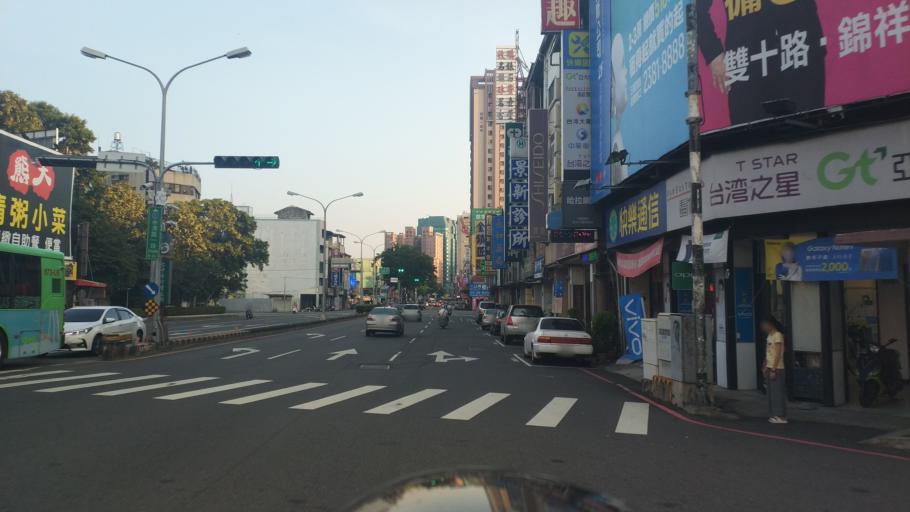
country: TW
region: Taiwan
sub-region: Taichung City
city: Taichung
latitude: 24.1593
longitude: 120.6756
